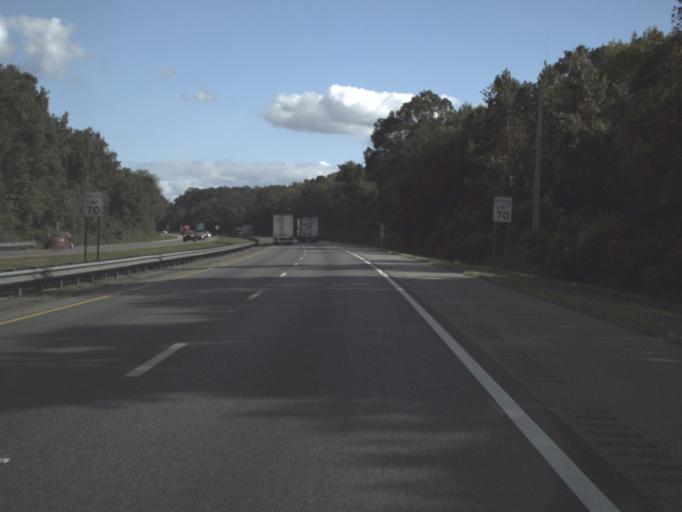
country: US
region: Florida
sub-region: Sumter County
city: Wildwood
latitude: 28.8511
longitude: -82.0846
